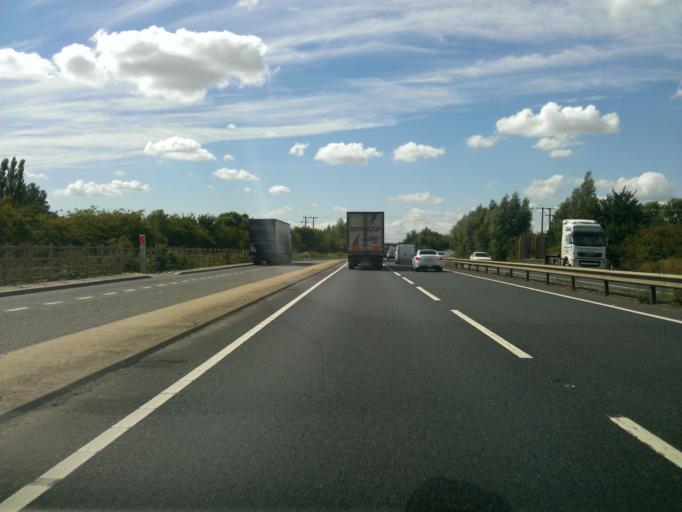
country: GB
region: England
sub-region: Cambridgeshire
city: Buckden
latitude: 52.3335
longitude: -0.2916
